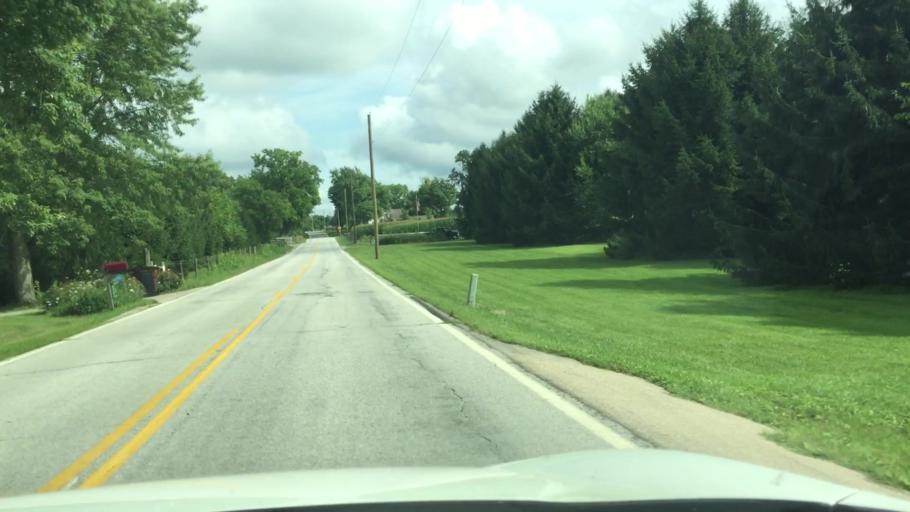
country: US
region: Ohio
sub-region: Clark County
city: Northridge
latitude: 39.9861
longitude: -83.6841
